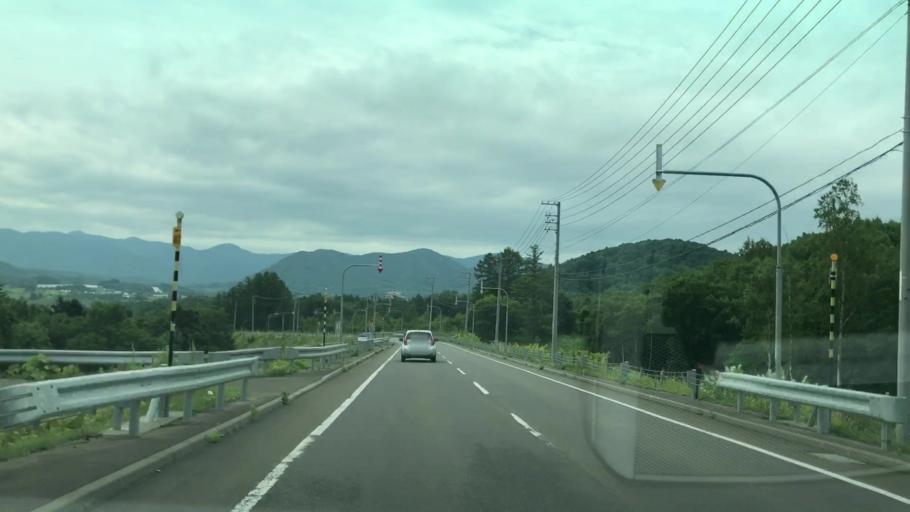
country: JP
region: Hokkaido
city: Yoichi
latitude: 43.1124
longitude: 140.8196
